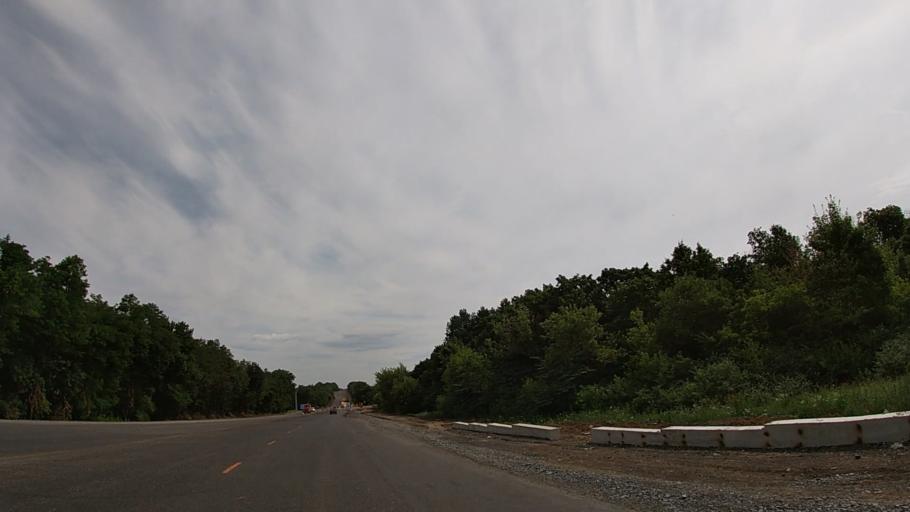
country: RU
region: Belgorod
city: Mayskiy
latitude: 50.4837
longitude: 36.4084
